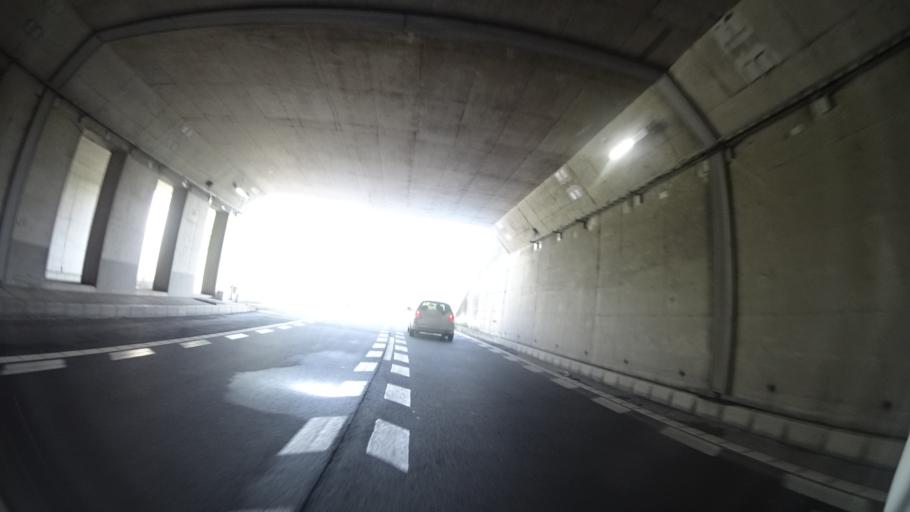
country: JP
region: Hyogo
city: Akashi
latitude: 34.6580
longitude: 135.0670
